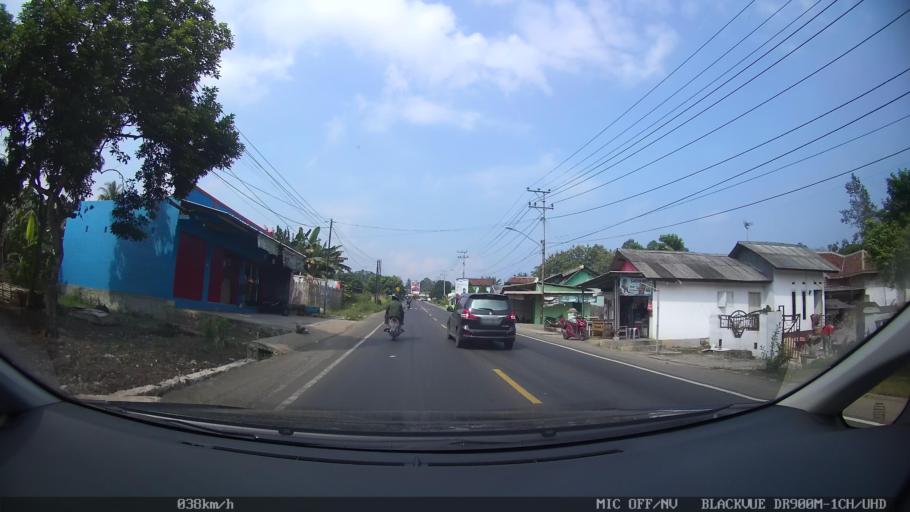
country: ID
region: Lampung
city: Natar
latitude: -5.3659
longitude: 105.1820
